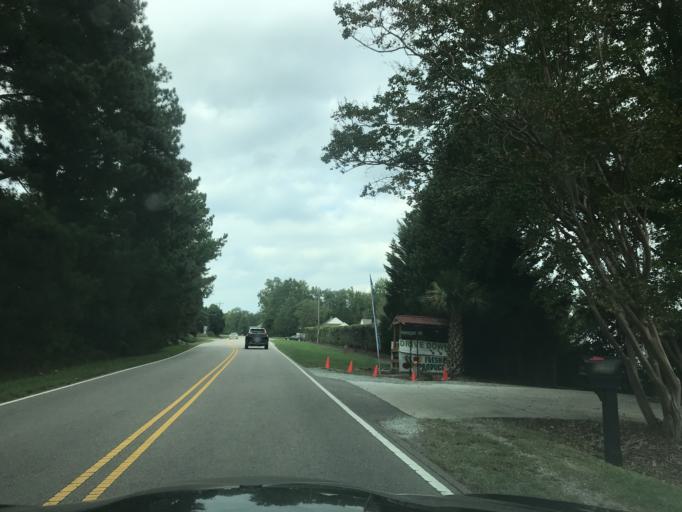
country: US
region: North Carolina
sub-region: Durham County
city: Durham
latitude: 35.9191
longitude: -78.9148
